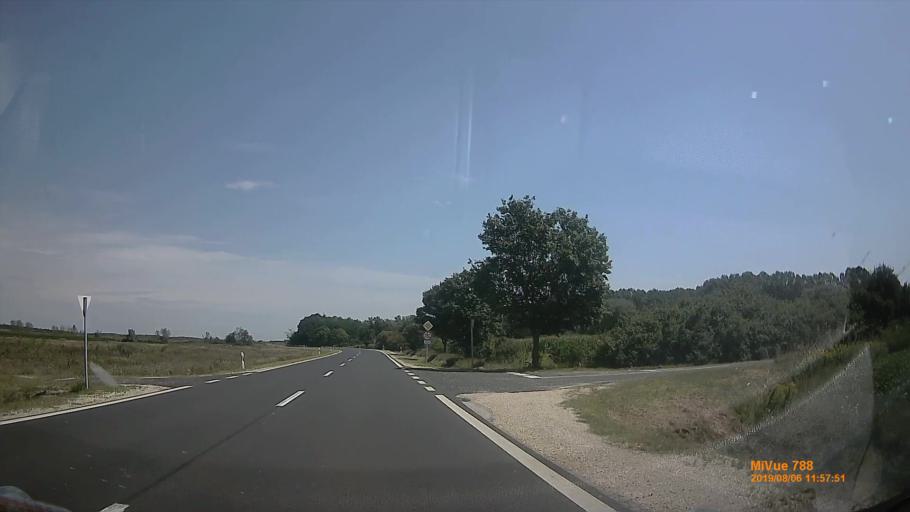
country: HU
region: Vas
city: Vasvar
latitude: 47.0619
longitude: 16.7166
